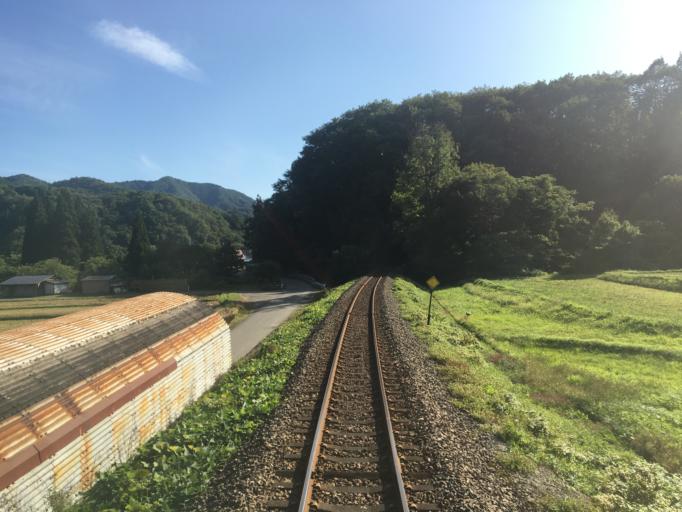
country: JP
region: Akita
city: Kakunodatemachi
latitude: 39.7536
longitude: 140.5987
